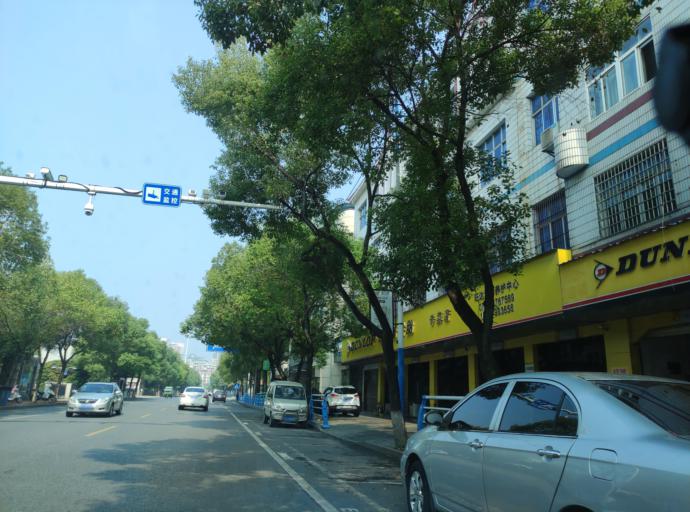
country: CN
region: Jiangxi Sheng
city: Pingxiang
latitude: 27.6432
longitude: 113.8553
